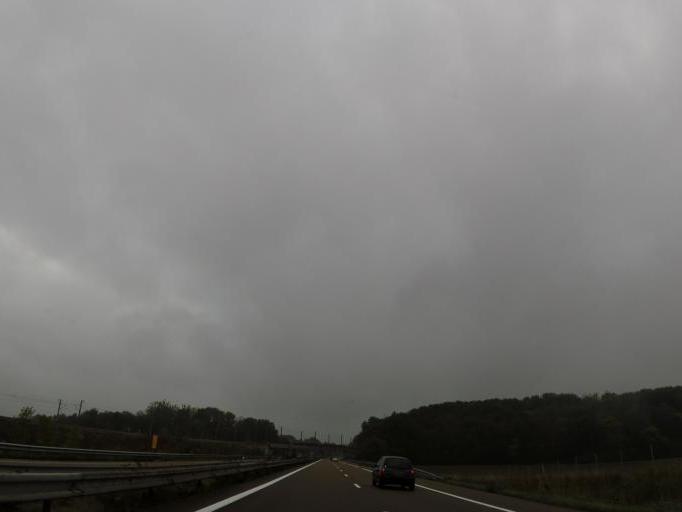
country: FR
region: Picardie
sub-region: Departement de l'Aisne
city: Montreuil-aux-Lions
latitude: 49.0431
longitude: 3.2541
